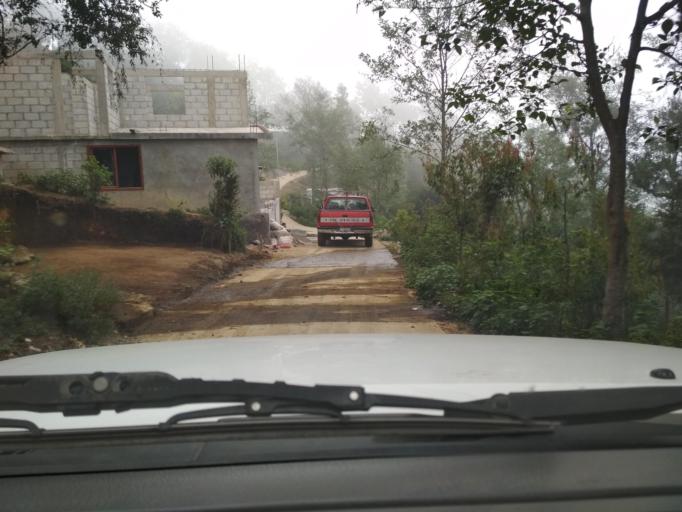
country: MX
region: Veracruz
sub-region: La Perla
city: Metlac Hernandez (Metlac Primero)
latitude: 18.9698
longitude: -97.1503
